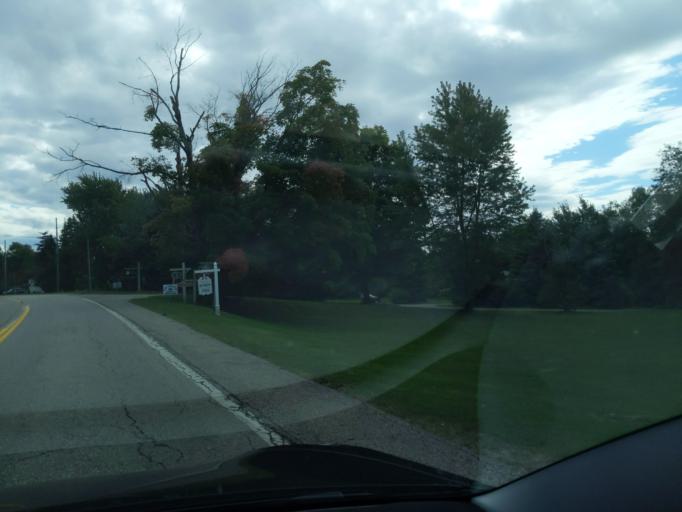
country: US
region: Michigan
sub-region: Kalkaska County
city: Rapid City
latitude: 44.9180
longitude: -85.2856
